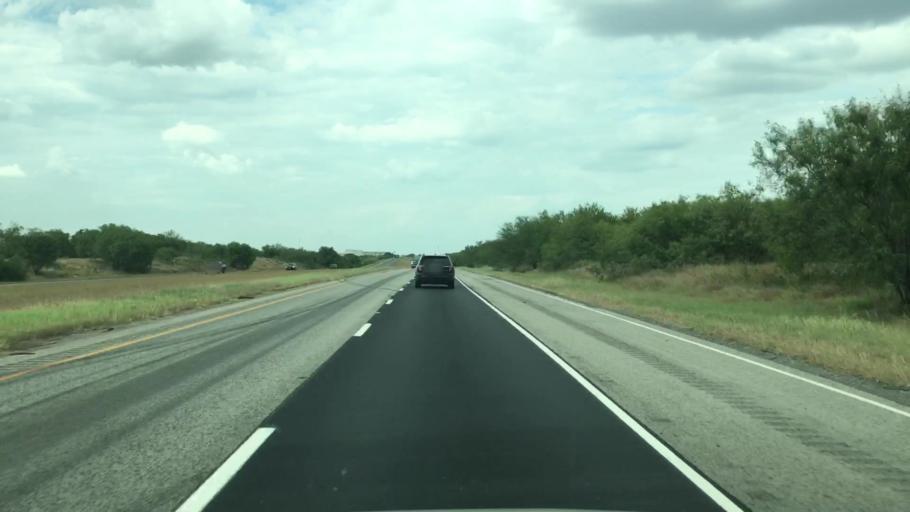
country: US
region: Texas
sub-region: Atascosa County
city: Pleasanton
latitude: 29.0786
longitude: -98.4328
